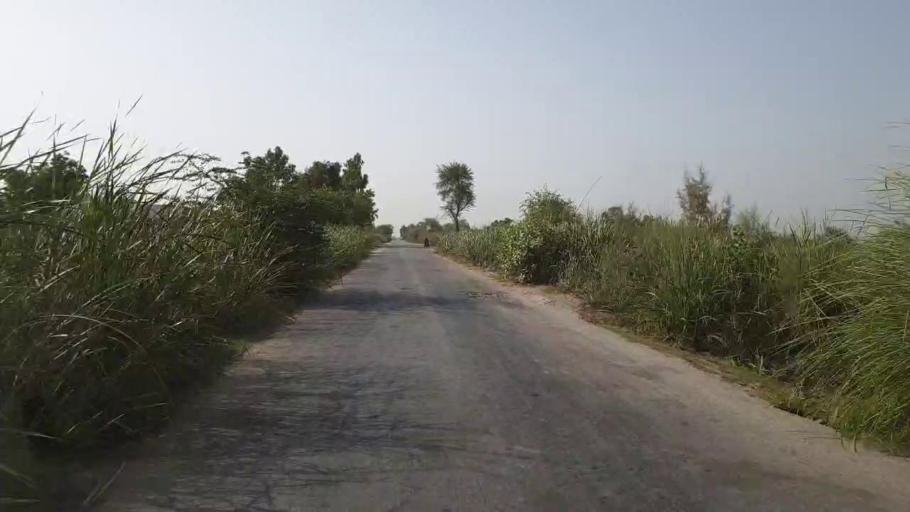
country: PK
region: Sindh
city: Khadro
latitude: 26.3335
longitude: 68.9288
